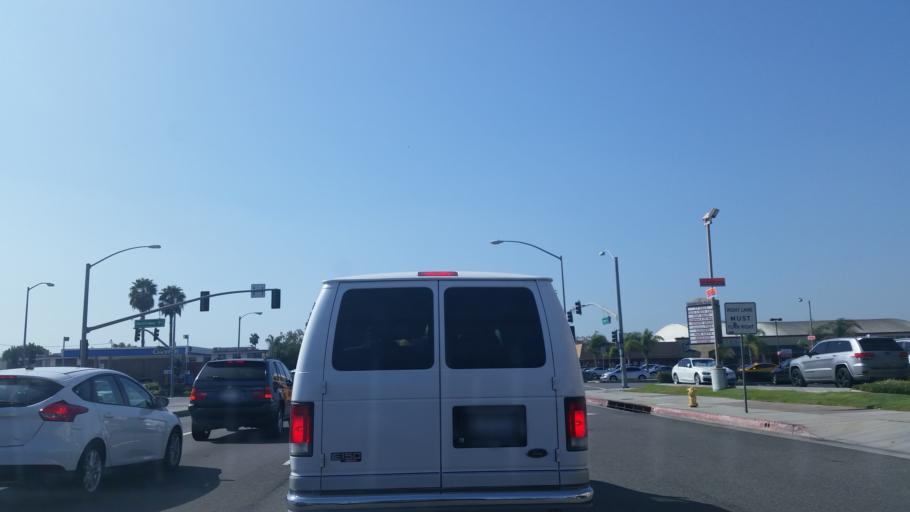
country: US
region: California
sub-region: Los Angeles County
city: Lakewood
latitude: 33.8604
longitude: -118.1243
